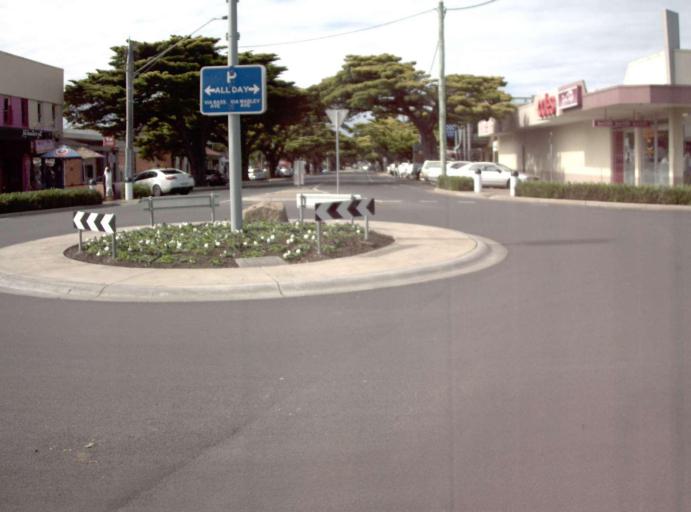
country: AU
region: Victoria
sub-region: Bass Coast
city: Cowes
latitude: -38.4501
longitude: 145.2390
